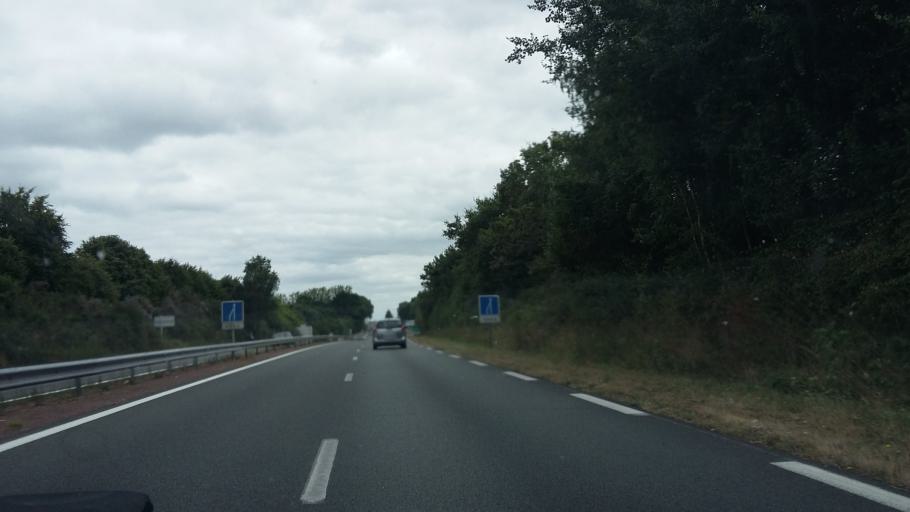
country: FR
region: Pays de la Loire
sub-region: Departement de la Vendee
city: La Roche-sur-Yon
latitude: 46.6870
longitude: -1.4566
